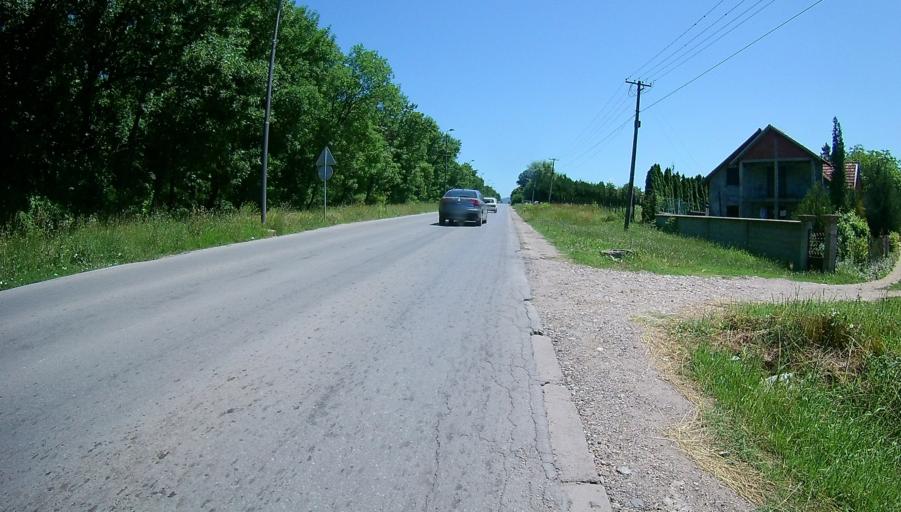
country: RS
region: Central Serbia
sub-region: Nisavski Okrug
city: Nis
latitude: 43.3045
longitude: 21.8687
